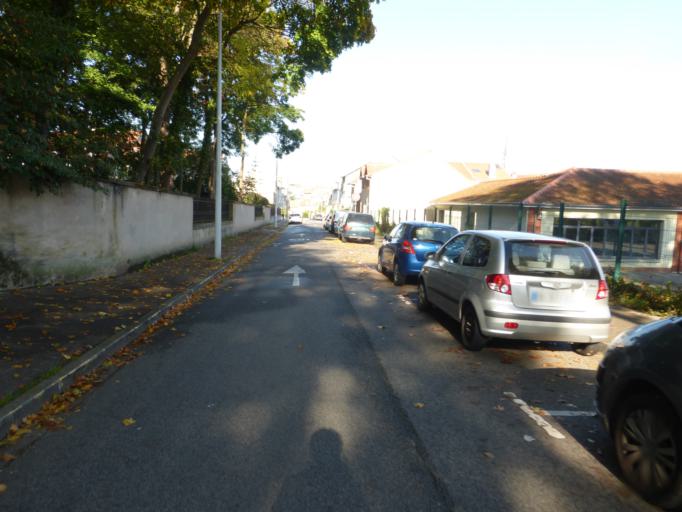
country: FR
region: Lorraine
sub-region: Departement de Meurthe-et-Moselle
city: Nancy
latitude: 48.6694
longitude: 6.1763
